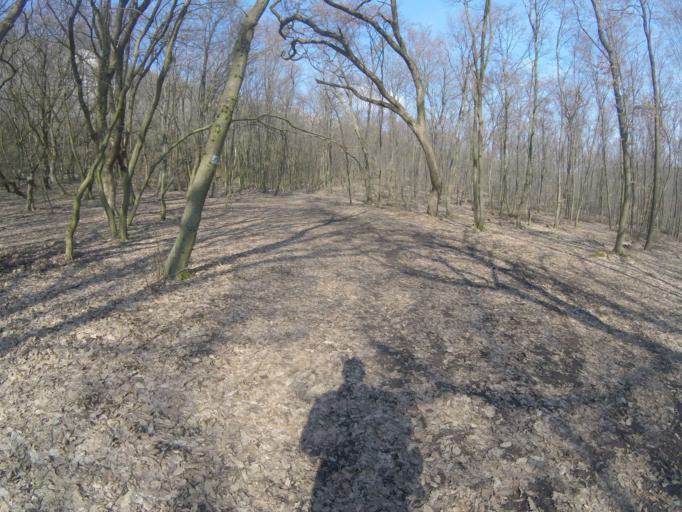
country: HU
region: Komarom-Esztergom
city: Nyergesujfalu
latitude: 47.7248
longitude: 18.5761
